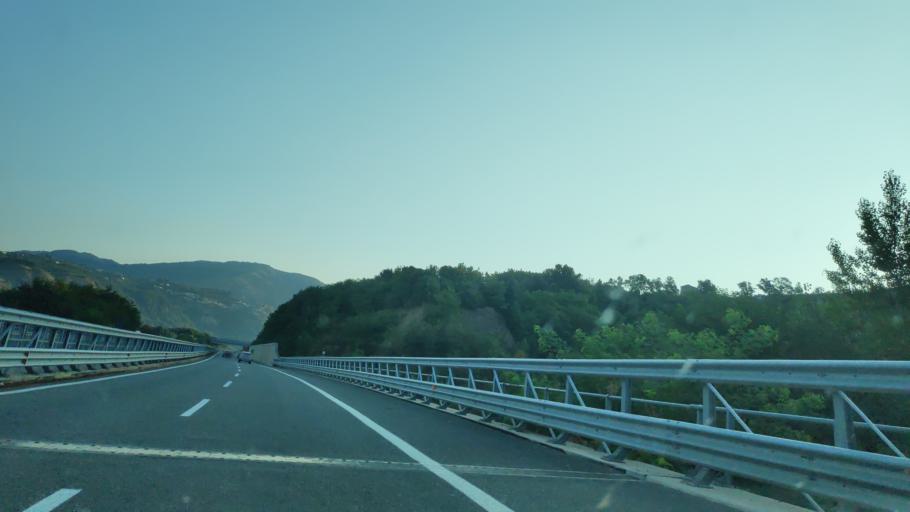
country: IT
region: Calabria
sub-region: Provincia di Catanzaro
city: Nocera Terinese
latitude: 39.0511
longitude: 16.1520
